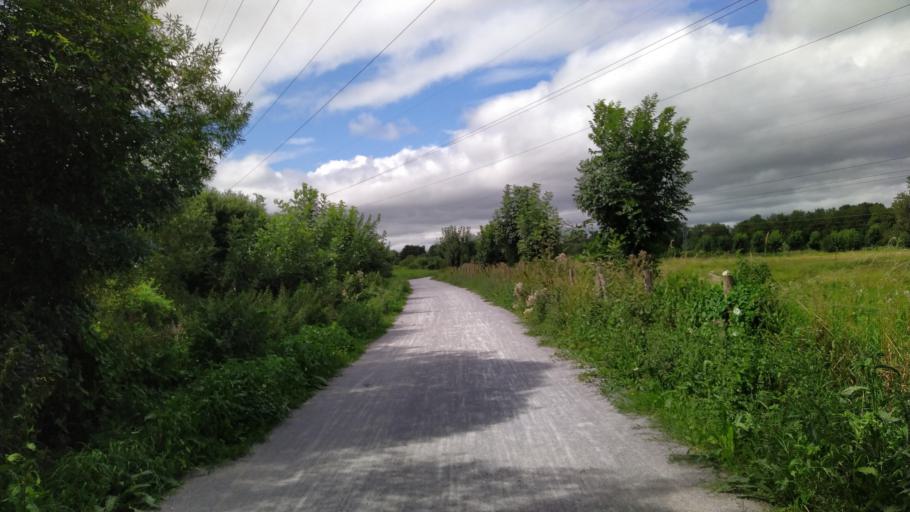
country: FR
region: Pays de la Loire
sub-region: Departement de la Loire-Atlantique
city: Bouguenais
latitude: 47.1817
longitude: -1.6236
